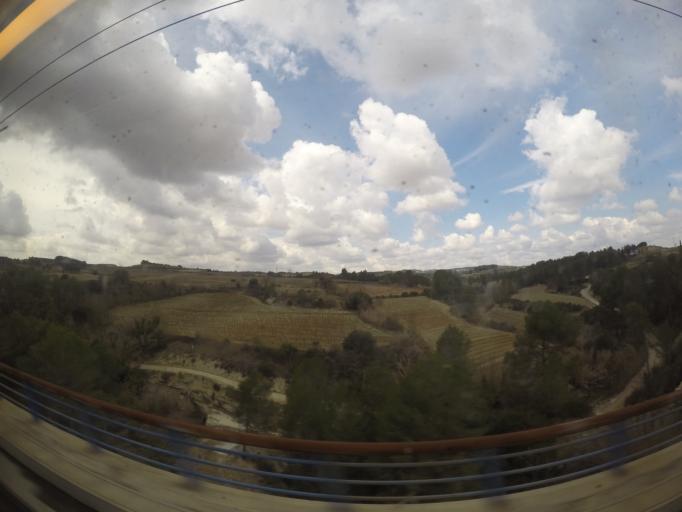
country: ES
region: Catalonia
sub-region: Provincia de Barcelona
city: Sant Llorenc d'Hortons
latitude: 41.4404
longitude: 1.8294
